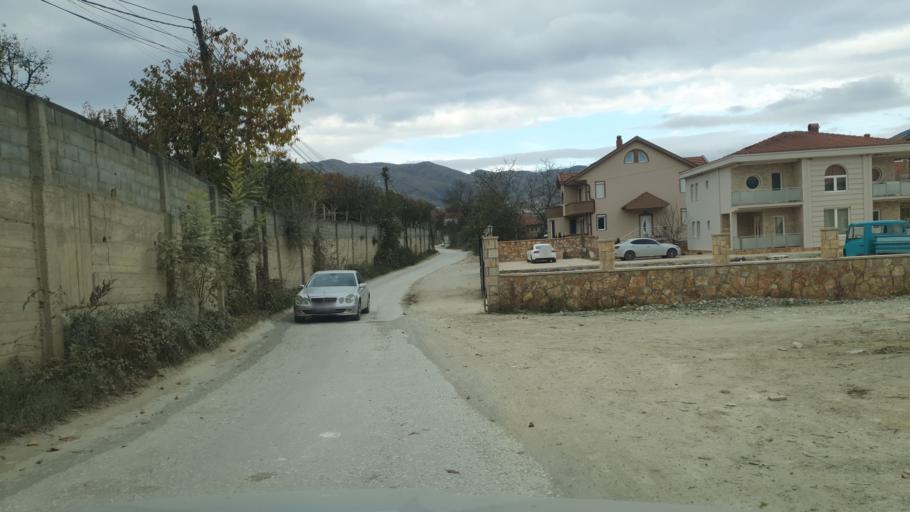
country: MK
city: Kondovo
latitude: 42.0317
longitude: 21.2839
